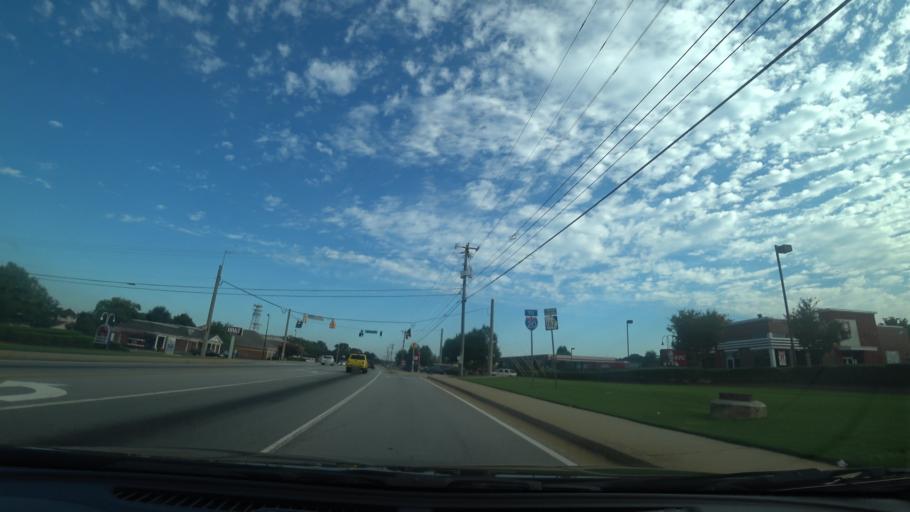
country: US
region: Georgia
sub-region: Rockdale County
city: Conyers
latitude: 33.6244
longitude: -83.9767
